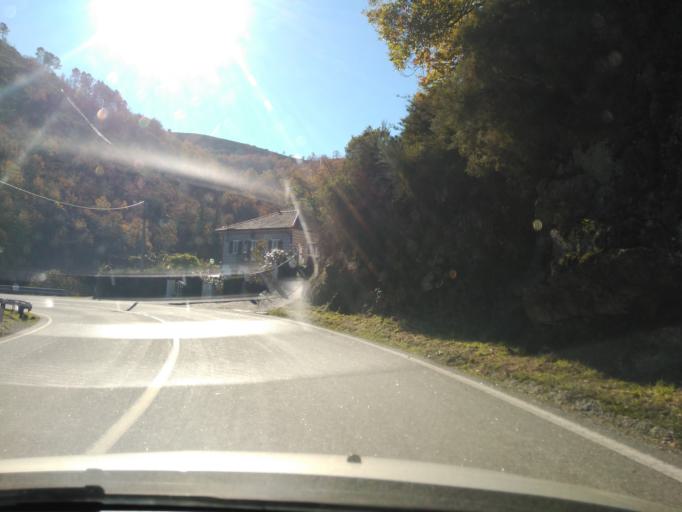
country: PT
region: Braga
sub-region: Cabeceiras de Basto
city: Cabeceiras de Basto
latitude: 41.6689
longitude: -7.9876
